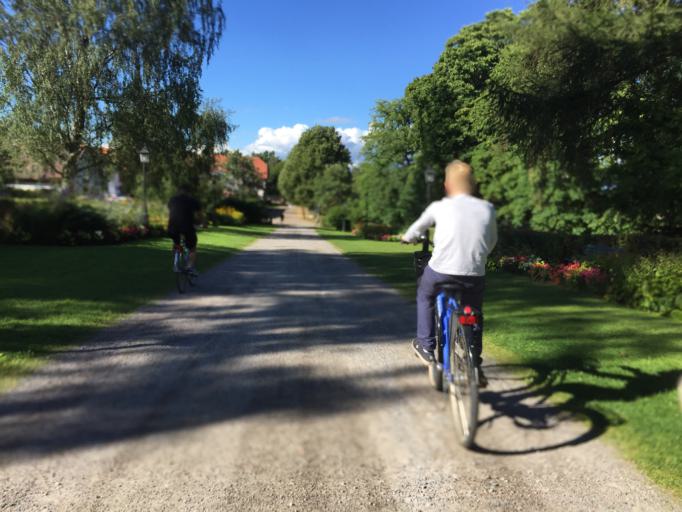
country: SE
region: OErebro
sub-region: Orebro Kommun
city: Orebro
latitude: 59.2703
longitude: 15.1489
